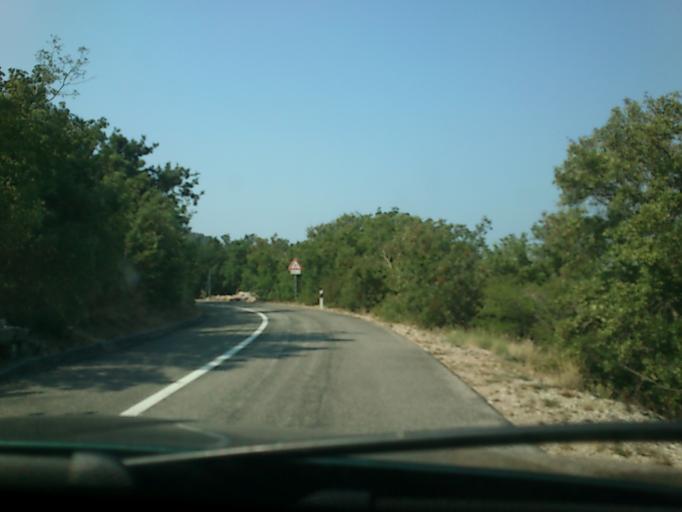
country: HR
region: Primorsko-Goranska
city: Banjol
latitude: 44.7079
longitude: 14.9033
